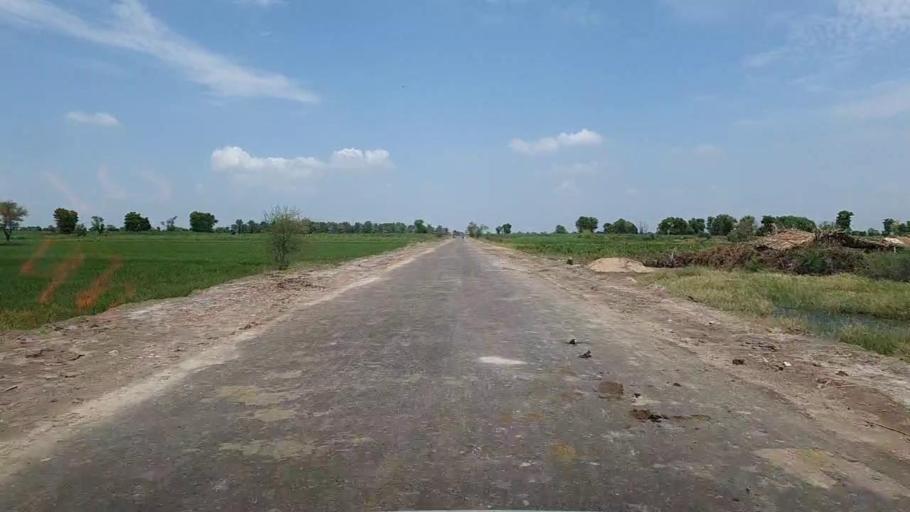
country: PK
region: Sindh
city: Bhiria
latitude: 26.9305
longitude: 68.2132
